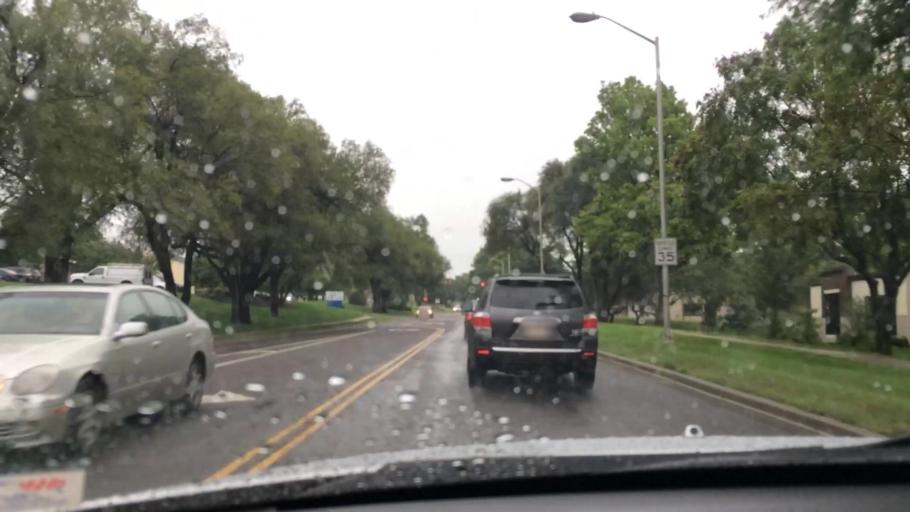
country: US
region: Kansas
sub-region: Johnson County
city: Overland Park
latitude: 38.9640
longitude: -94.6653
